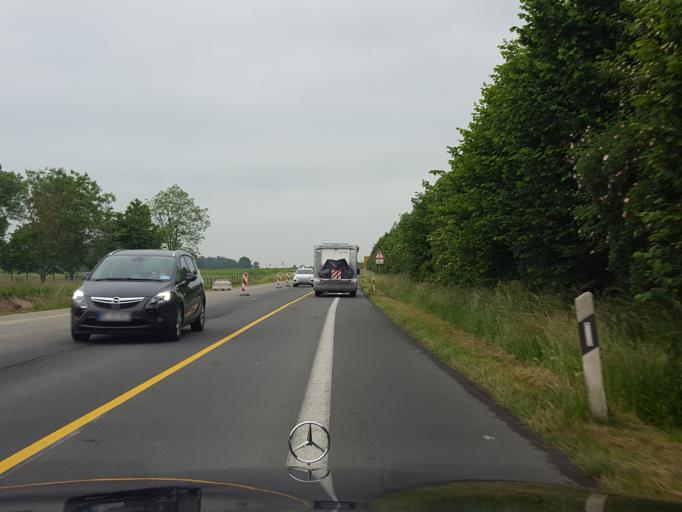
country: DE
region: North Rhine-Westphalia
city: Olfen
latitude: 51.6993
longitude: 7.3751
